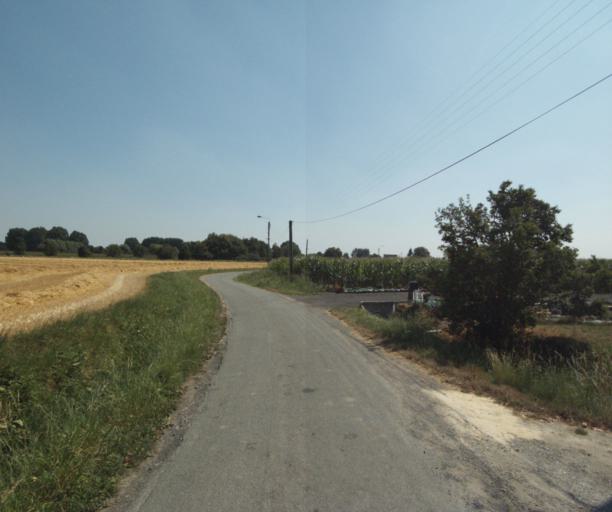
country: FR
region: Nord-Pas-de-Calais
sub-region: Departement du Nord
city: Comines
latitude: 50.7512
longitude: 3.0205
